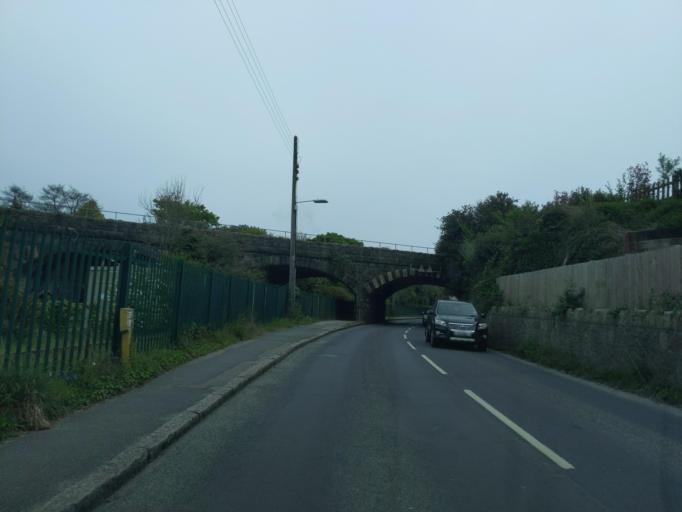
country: GB
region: England
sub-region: Cornwall
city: Par
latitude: 50.3494
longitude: -4.7069
